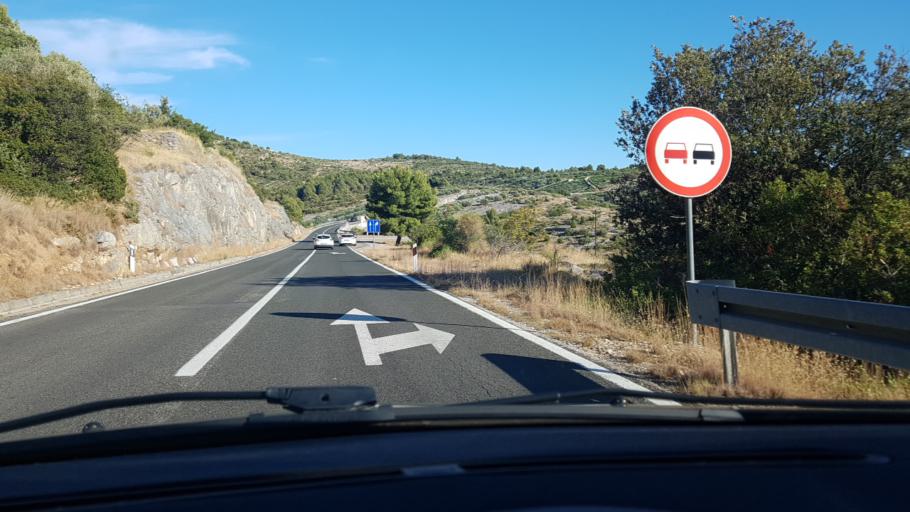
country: HR
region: Sibensko-Kniniska
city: Primosten
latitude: 43.5708
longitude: 15.9444
